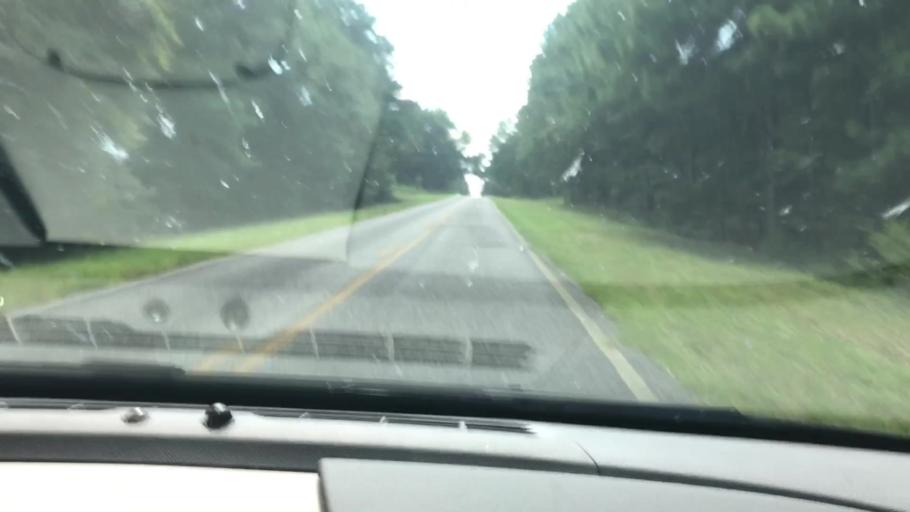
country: US
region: Georgia
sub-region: Quitman County
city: Georgetown
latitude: 31.7483
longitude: -85.0779
